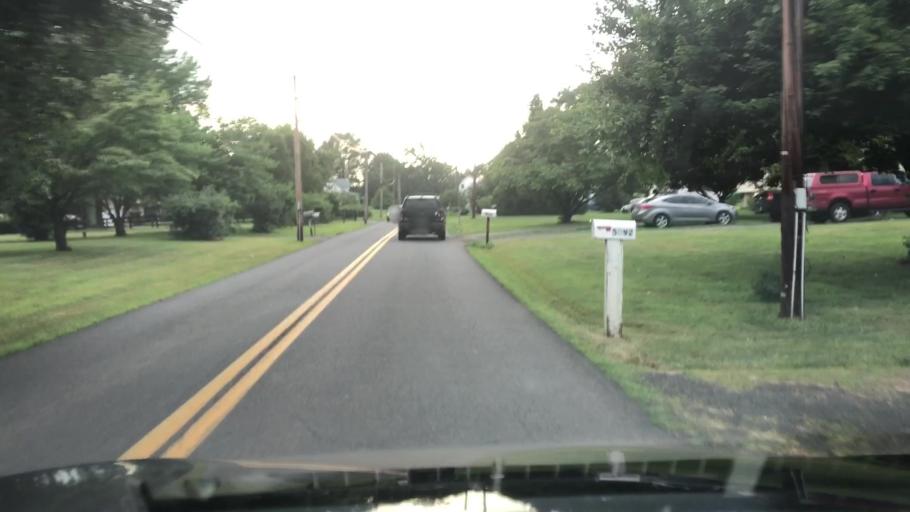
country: US
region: Virginia
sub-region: Fauquier County
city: New Baltimore
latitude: 38.7645
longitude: -77.7144
